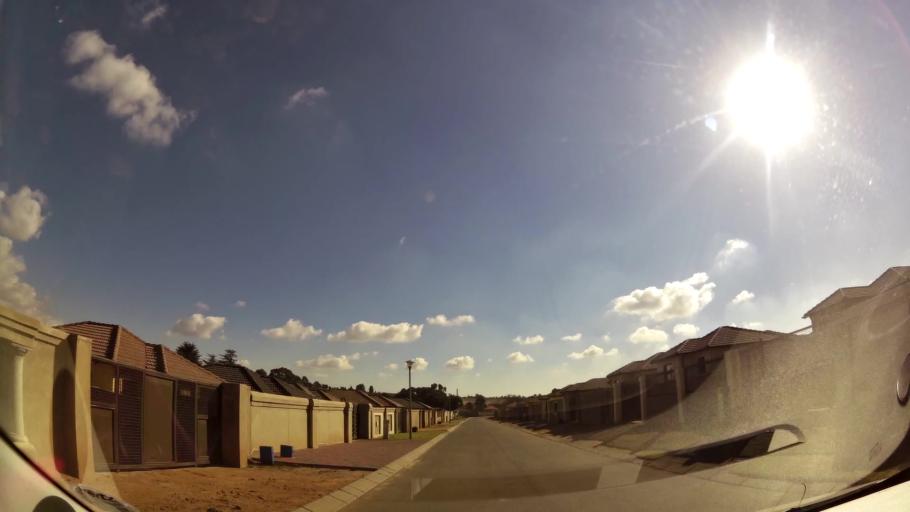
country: ZA
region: Gauteng
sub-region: City of Johannesburg Metropolitan Municipality
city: Roodepoort
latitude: -26.1415
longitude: 27.8230
